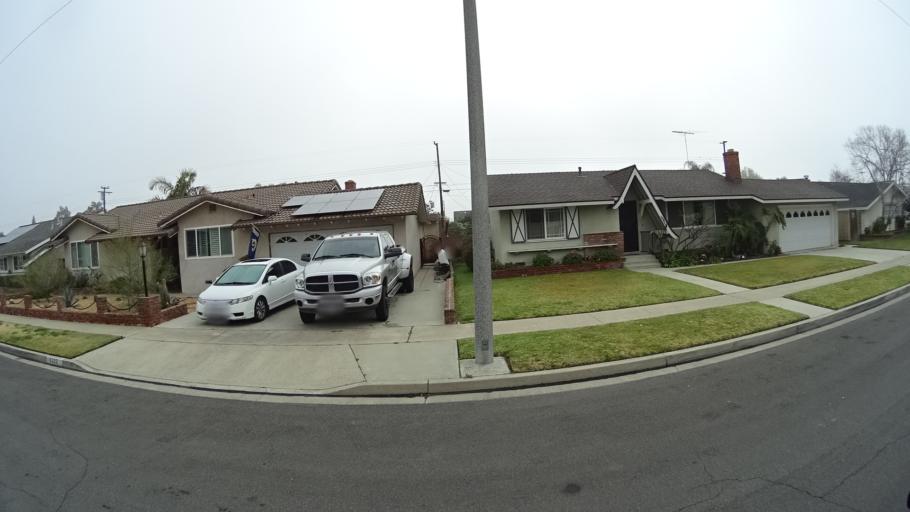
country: US
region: California
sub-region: Orange County
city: Stanton
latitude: 33.8145
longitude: -118.0051
